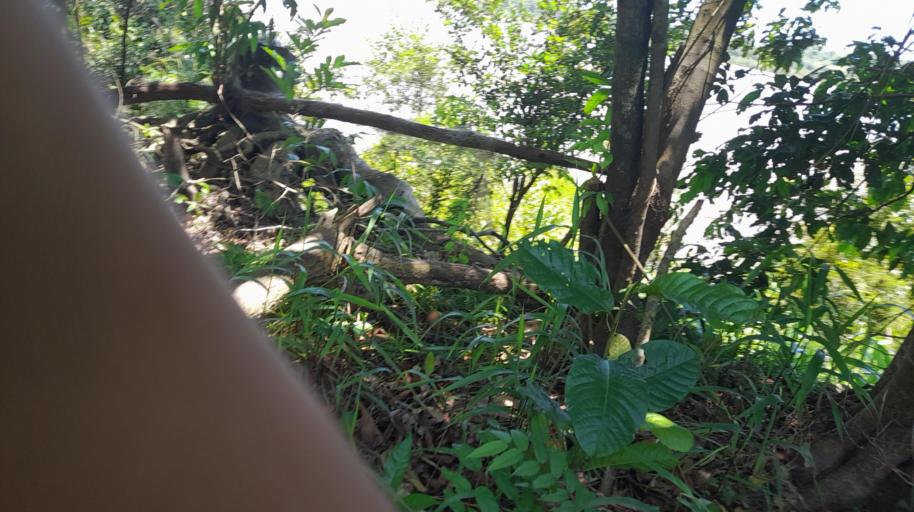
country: PE
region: Ucayali
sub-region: Provincia de Coronel Portillo
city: Puerto Callao
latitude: -8.2628
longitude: -74.6395
